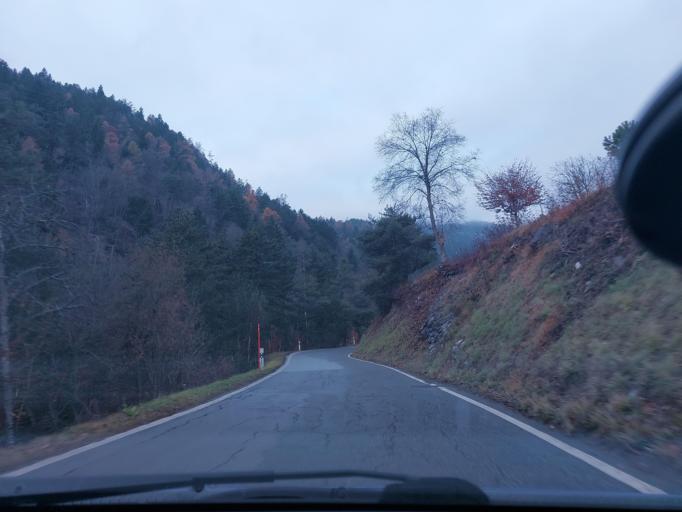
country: CH
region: Valais
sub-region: Conthey District
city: Chamoson
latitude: 46.2072
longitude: 7.2109
